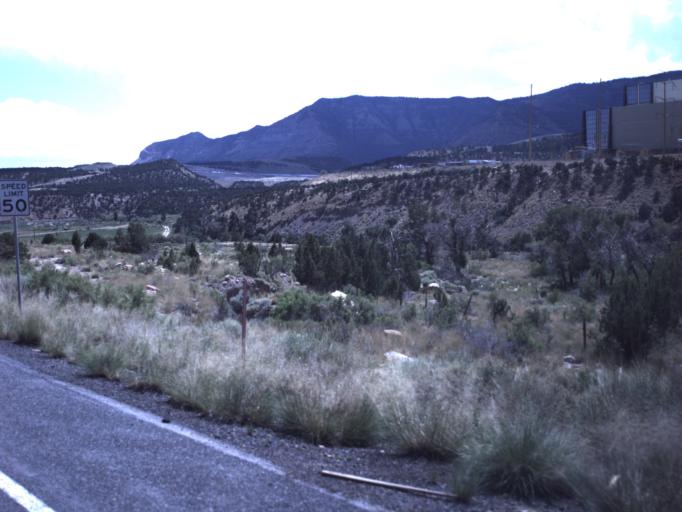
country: US
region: Utah
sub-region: Emery County
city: Huntington
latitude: 39.3838
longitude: -111.0756
